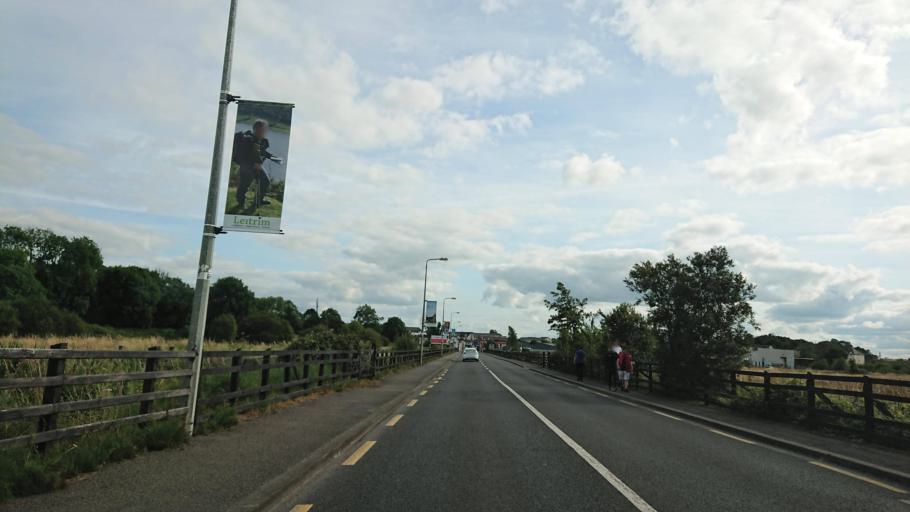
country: IE
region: Connaught
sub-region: County Leitrim
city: Carrick-on-Shannon
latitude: 53.9519
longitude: -8.0906
